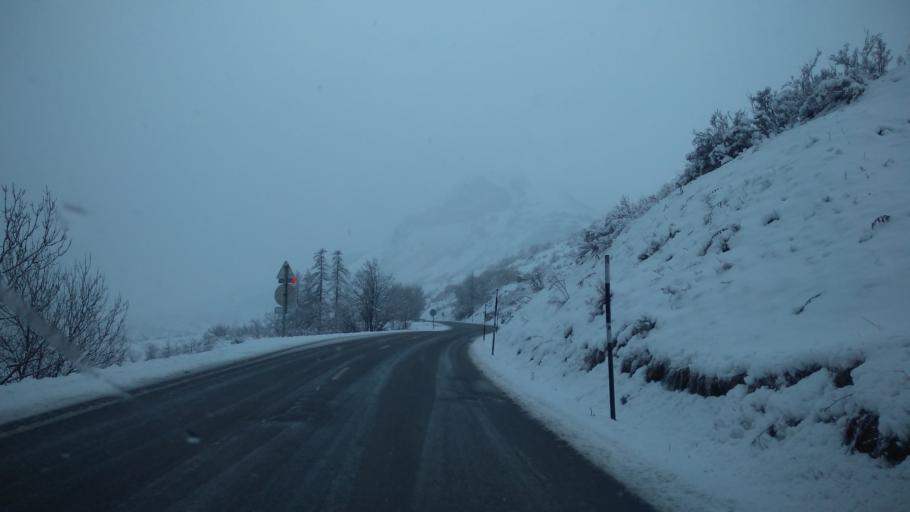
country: FR
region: Provence-Alpes-Cote d'Azur
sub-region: Departement des Hautes-Alpes
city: Le Monetier-les-Bains
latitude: 45.0096
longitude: 6.4708
